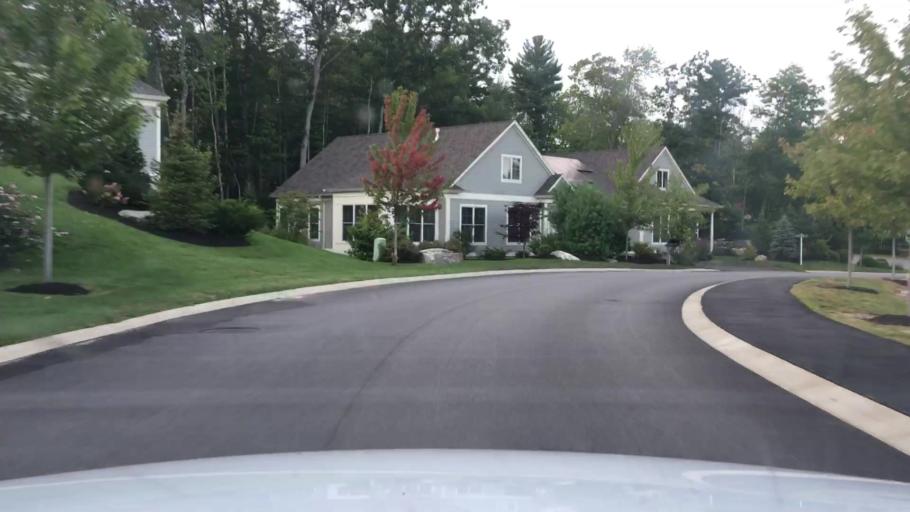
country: US
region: Maine
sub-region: Cumberland County
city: Falmouth
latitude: 43.7251
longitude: -70.2479
